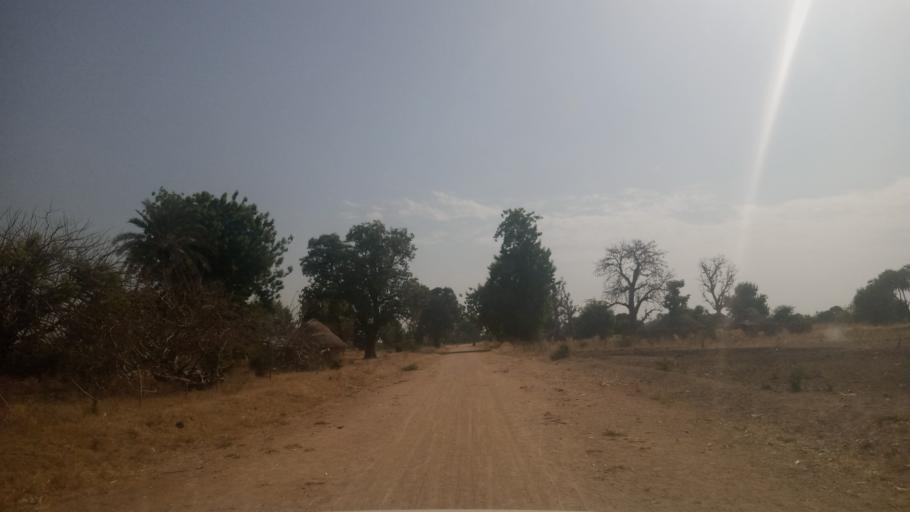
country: NG
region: Adamawa
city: Mayo Belwa
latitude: 9.0773
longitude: 12.0355
